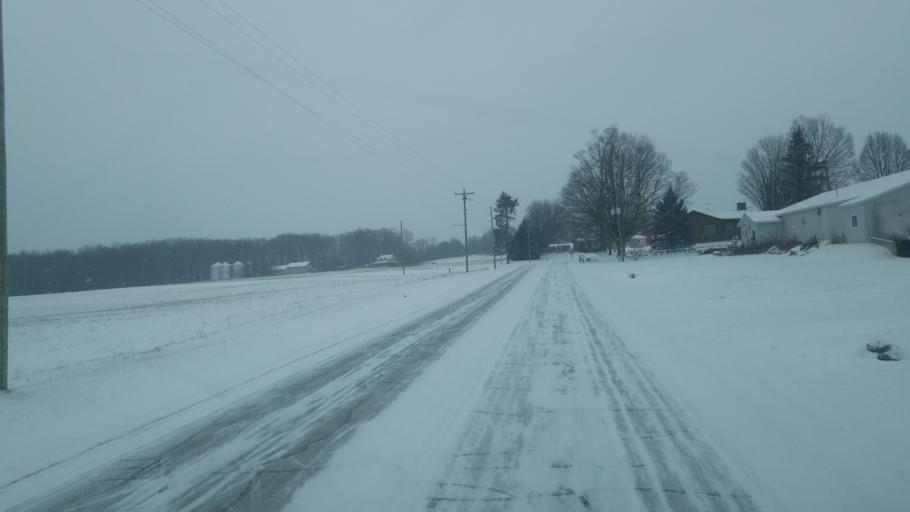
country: US
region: Michigan
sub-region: Osceola County
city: Reed City
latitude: 43.8204
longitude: -85.4040
